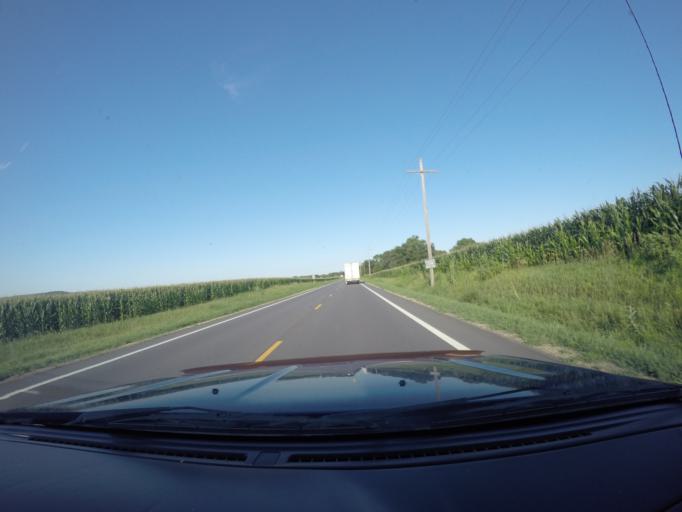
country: US
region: Kansas
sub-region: Douglas County
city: Lawrence
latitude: 39.0006
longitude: -95.2145
